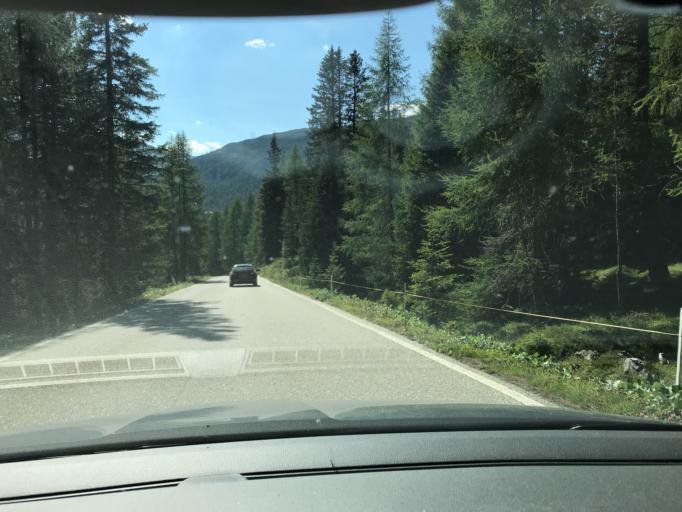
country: IT
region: Trentino-Alto Adige
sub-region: Bolzano
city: Sesto
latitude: 46.6073
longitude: 12.2779
